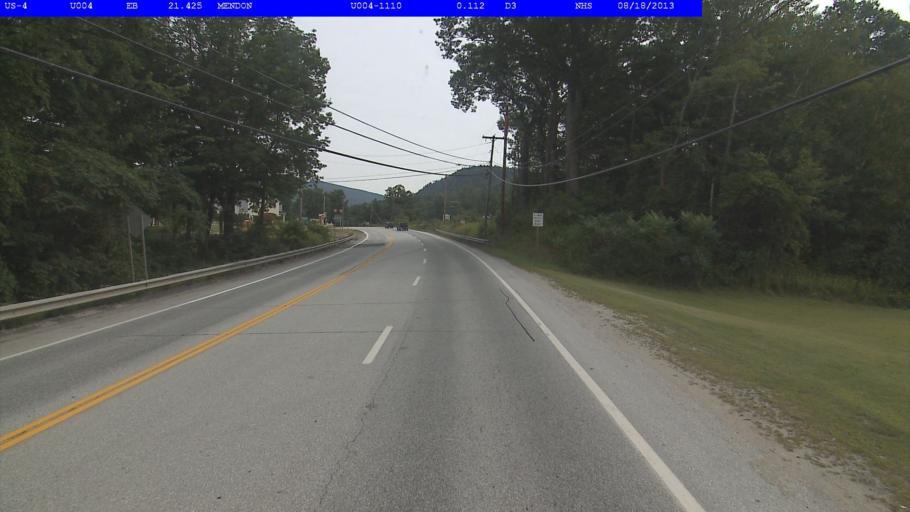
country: US
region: Vermont
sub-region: Rutland County
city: Rutland
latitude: 43.6360
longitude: -72.9358
